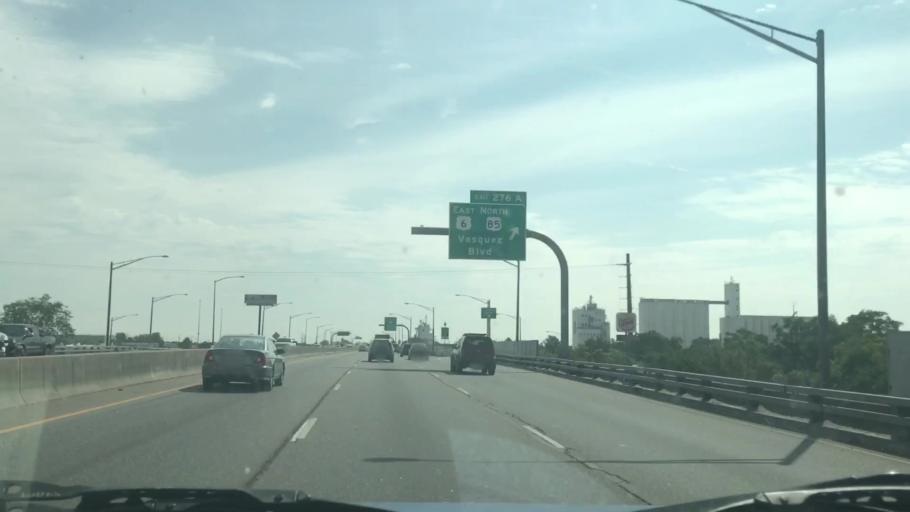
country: US
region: Colorado
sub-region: Adams County
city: Commerce City
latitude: 39.7798
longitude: -104.9552
